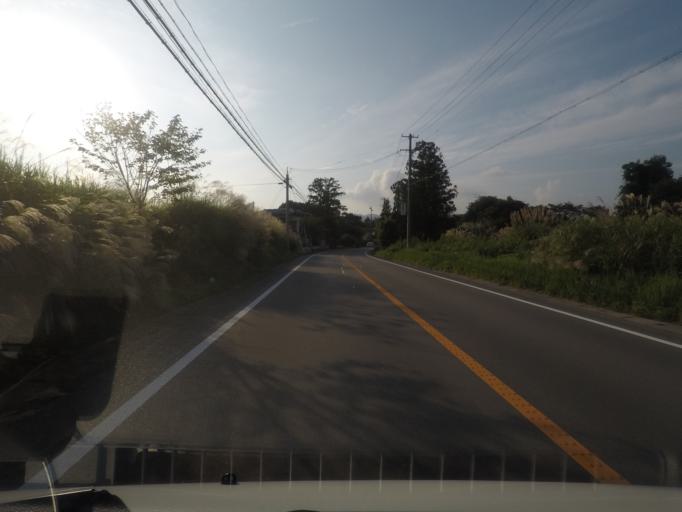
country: JP
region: Fukushima
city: Namie
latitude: 37.4997
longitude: 140.9509
